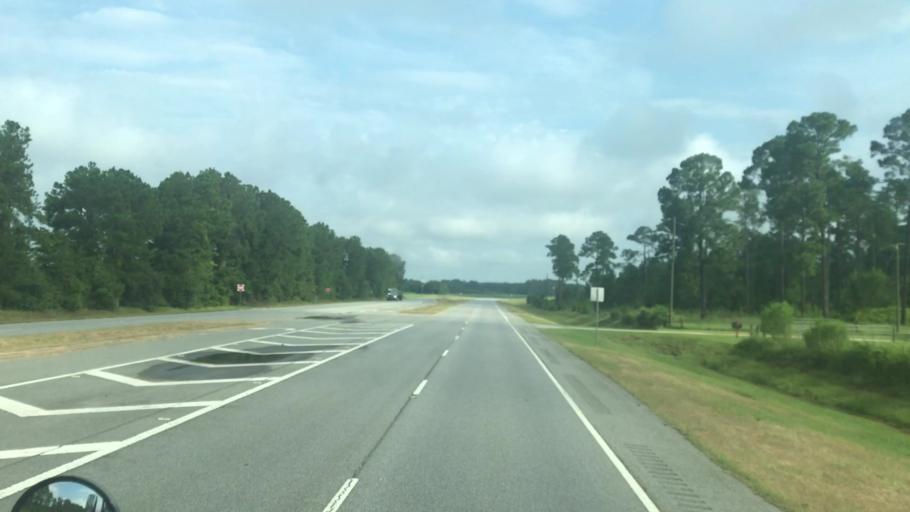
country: US
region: Georgia
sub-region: Miller County
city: Colquitt
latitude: 31.2123
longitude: -84.7753
